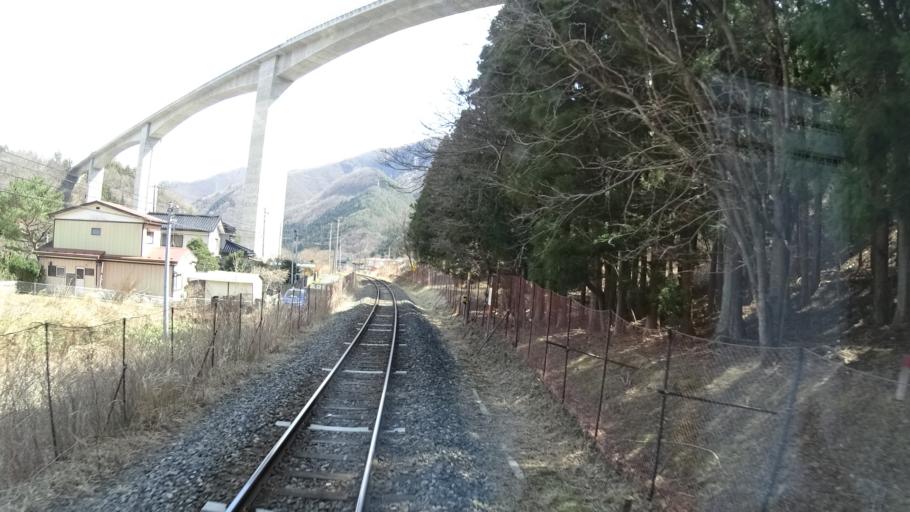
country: JP
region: Iwate
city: Kamaishi
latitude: 39.2523
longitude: 141.7531
